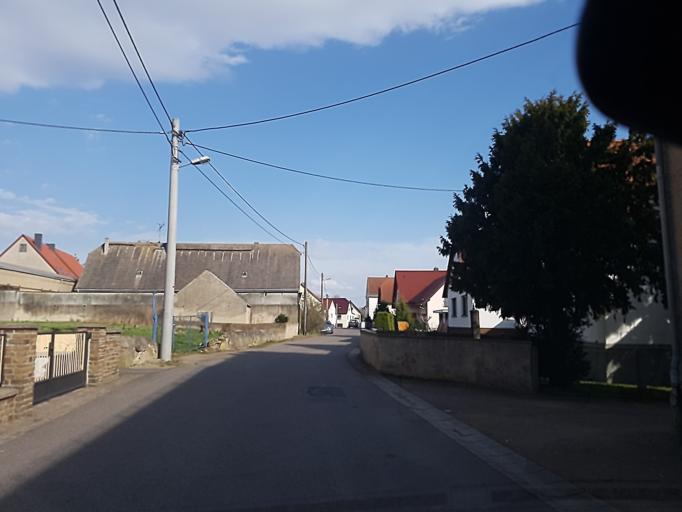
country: DE
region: Saxony
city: Oschatz
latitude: 51.2877
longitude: 13.1411
